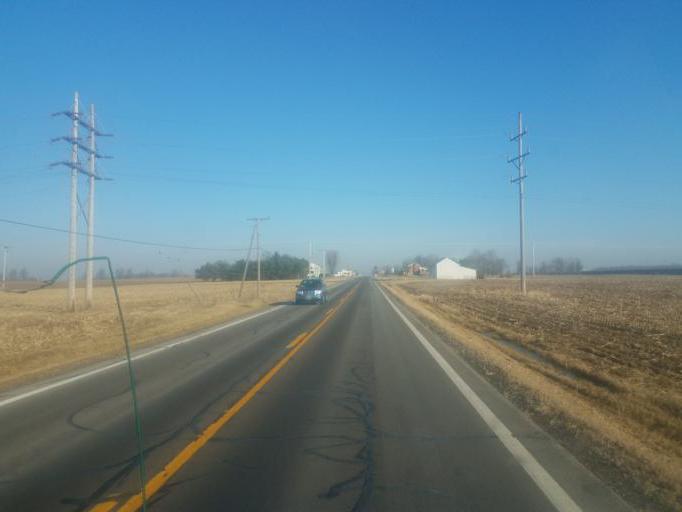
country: US
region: Ohio
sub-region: Crawford County
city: Bucyrus
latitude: 40.9635
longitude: -82.9375
